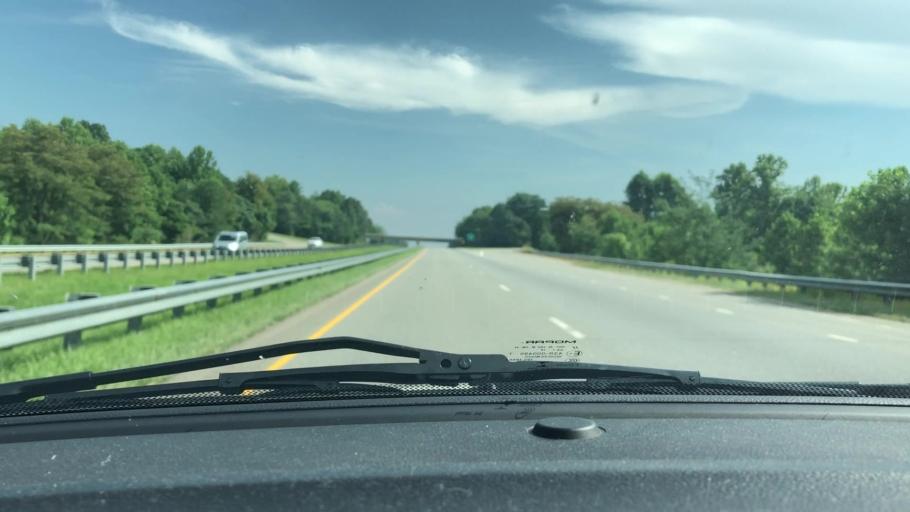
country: US
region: North Carolina
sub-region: Rockingham County
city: Stoneville
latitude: 36.5059
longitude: -79.9208
